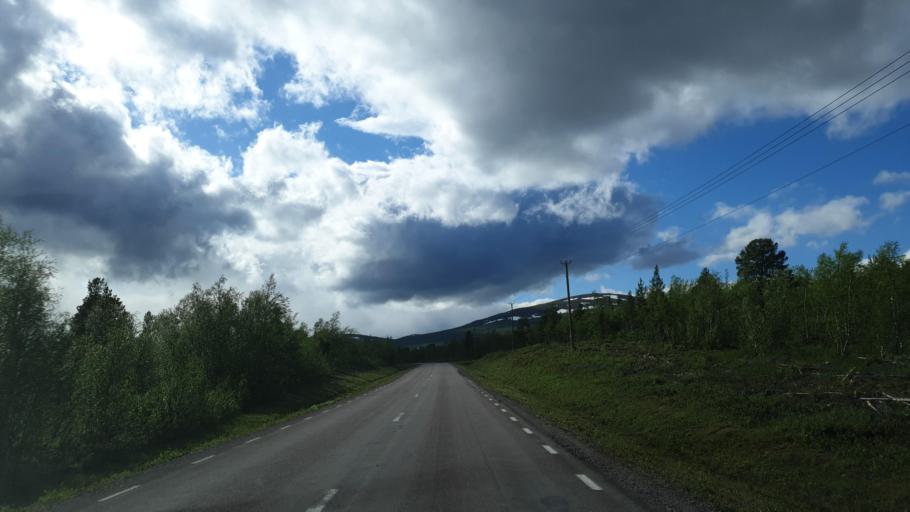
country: SE
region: Norrbotten
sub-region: Kiruna Kommun
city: Kiruna
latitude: 67.8707
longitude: 19.2495
